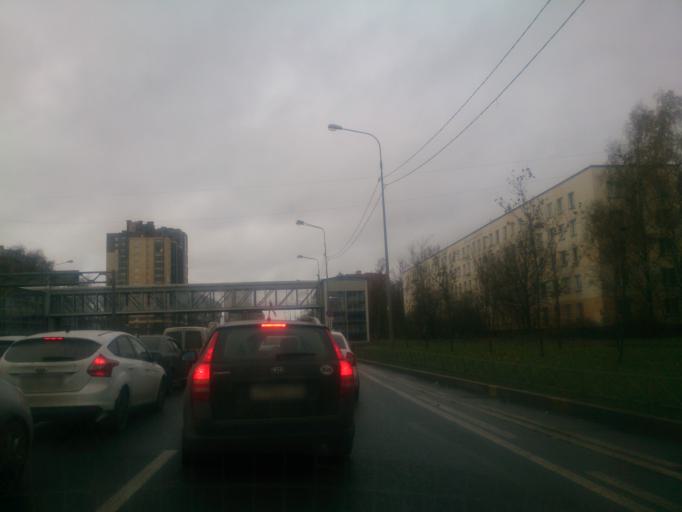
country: RU
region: St.-Petersburg
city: Dachnoye
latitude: 59.8385
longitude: 30.2618
